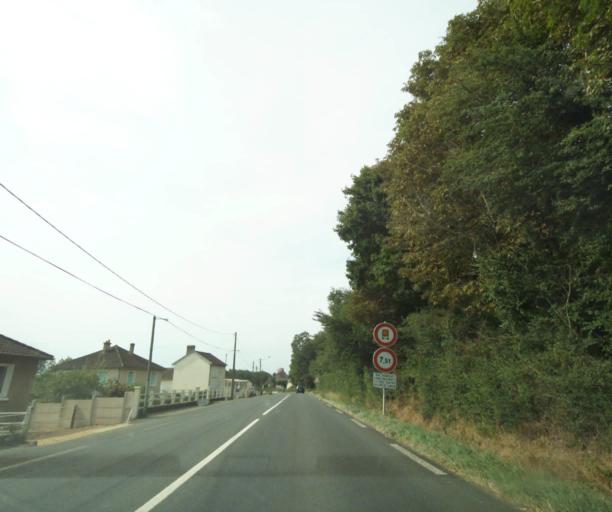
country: FR
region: Centre
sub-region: Departement d'Indre-et-Loire
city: Saint-Christophe-sur-le-Nais
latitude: 47.6615
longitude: 0.4764
